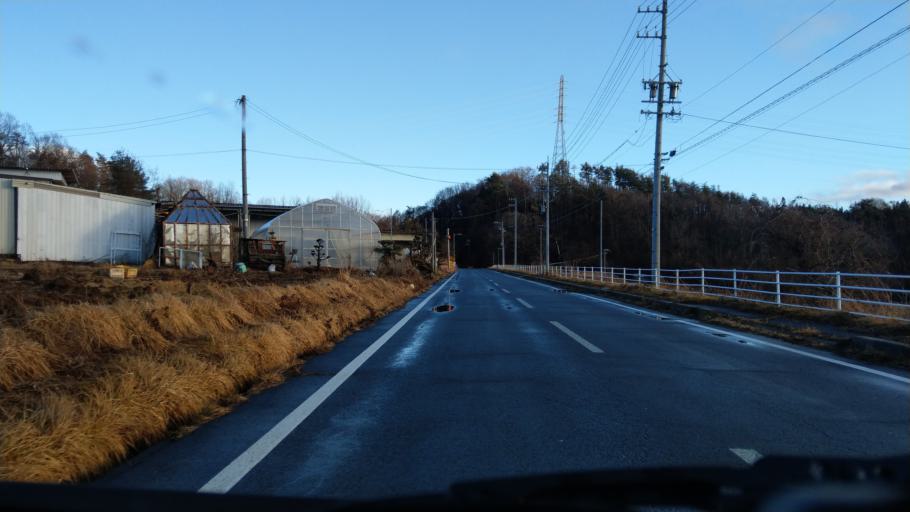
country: JP
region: Nagano
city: Komoro
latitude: 36.2974
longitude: 138.4131
